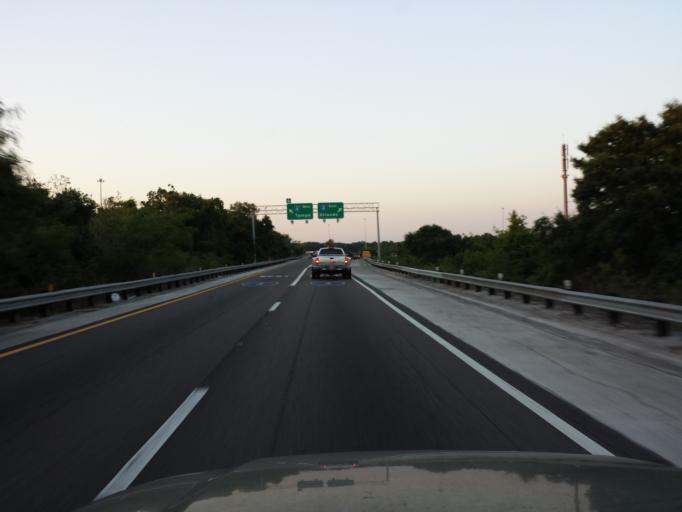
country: US
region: Florida
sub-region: Hillsborough County
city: Mango
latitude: 27.9982
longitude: -82.3257
